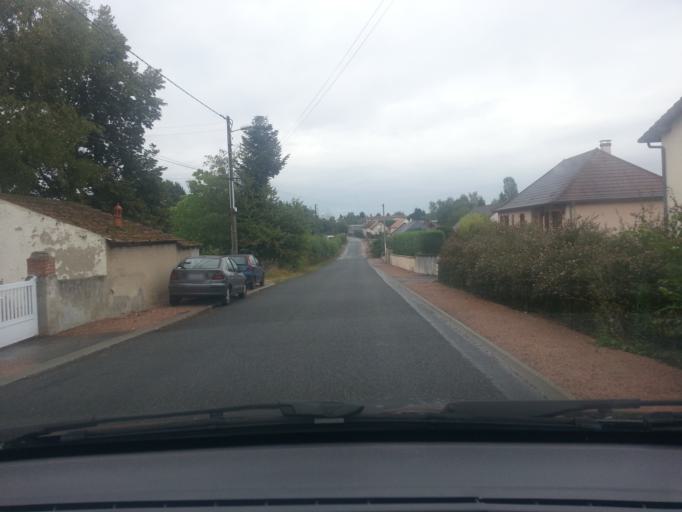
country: FR
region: Bourgogne
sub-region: Departement de Saone-et-Loire
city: Montchanin
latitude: 46.7423
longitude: 4.4594
